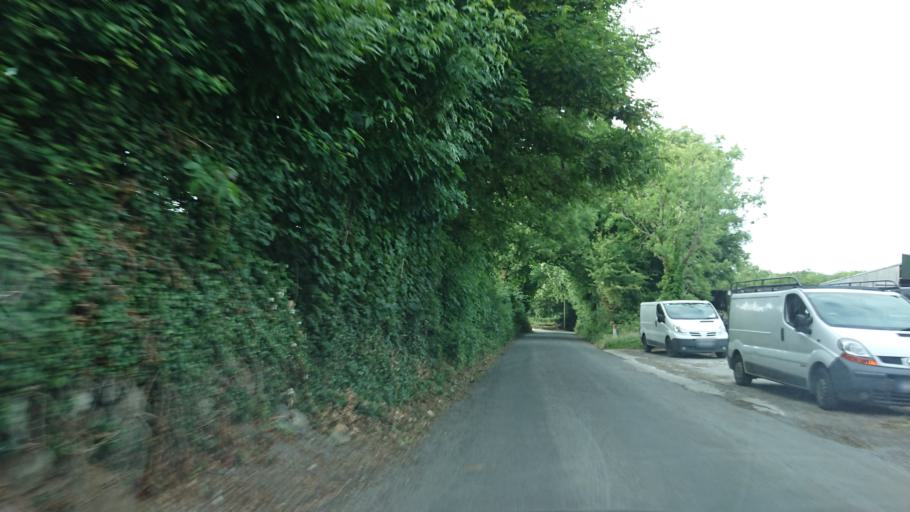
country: IE
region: Munster
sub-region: Waterford
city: Tra Mhor
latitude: 52.2166
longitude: -7.1863
